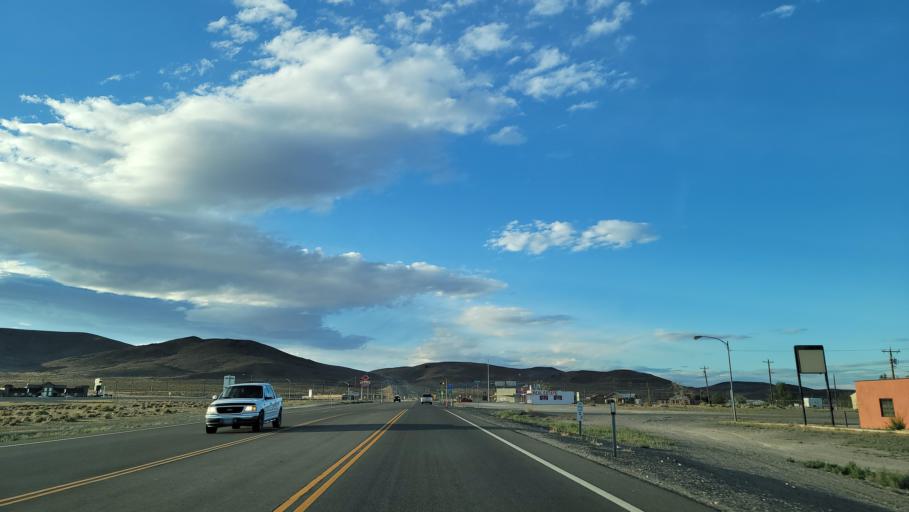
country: US
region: Nevada
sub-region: Lyon County
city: Silver Springs
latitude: 39.4124
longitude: -119.2258
